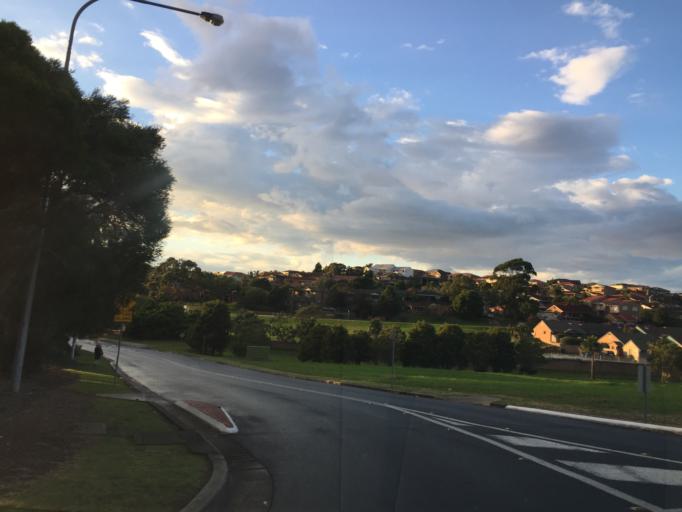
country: AU
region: New South Wales
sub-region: Shellharbour
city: Barrack Heights
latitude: -34.5670
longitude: 150.8377
